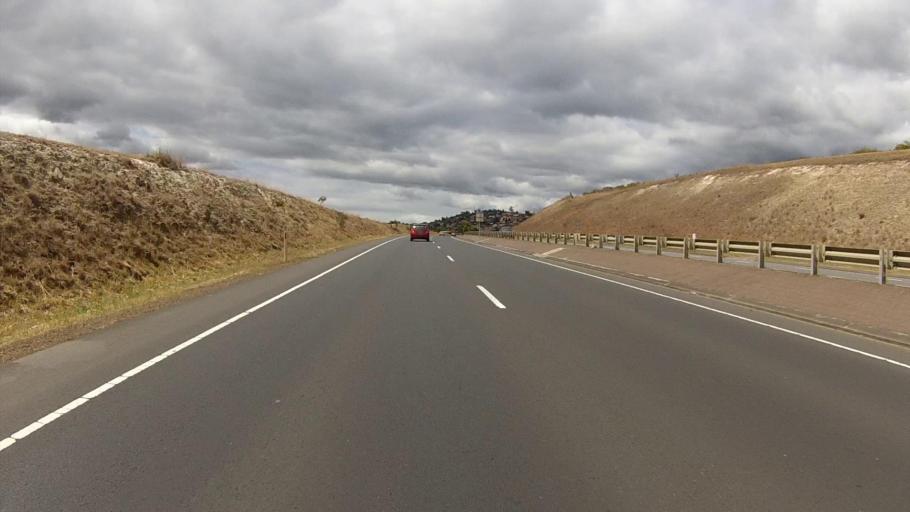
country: AU
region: Tasmania
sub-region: Glenorchy
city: Granton
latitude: -42.7602
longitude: 147.2328
